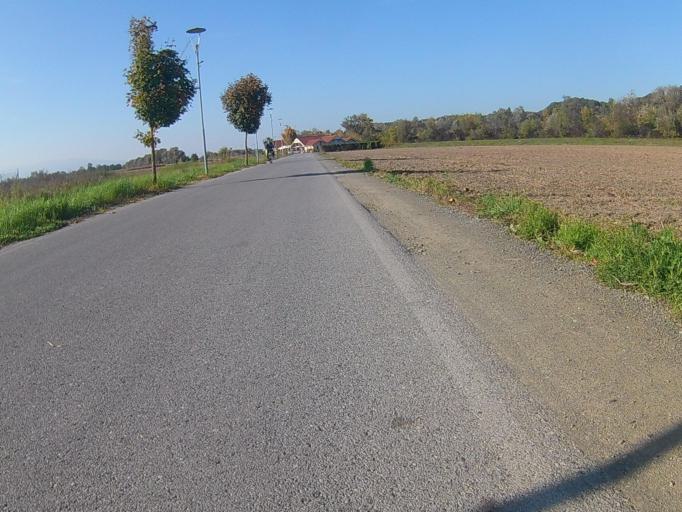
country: SI
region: Hajdina
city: Spodnja Hajdina
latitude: 46.4239
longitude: 15.8524
